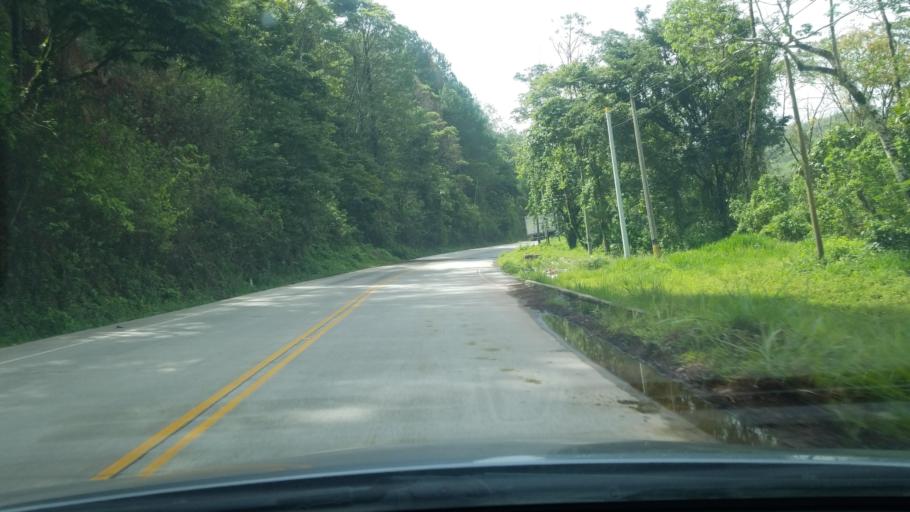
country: HN
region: Copan
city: San Jeronimo
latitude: 14.9319
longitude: -88.9427
